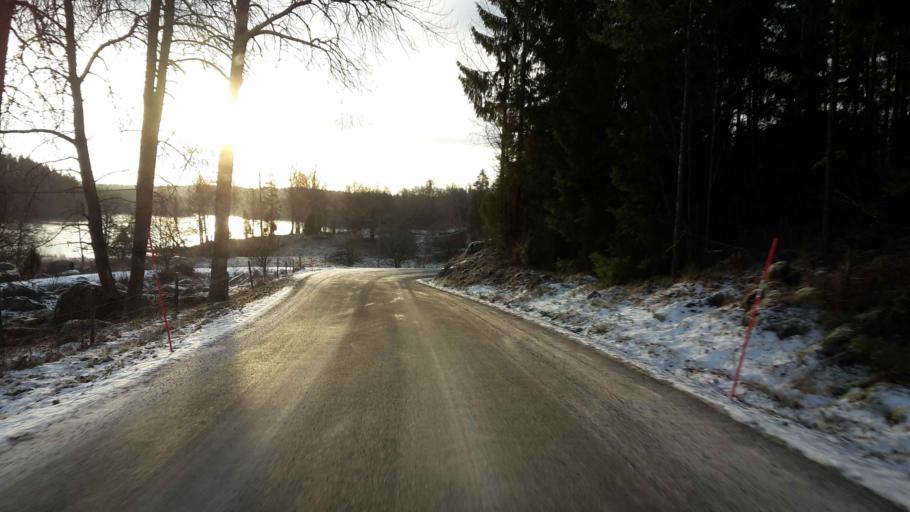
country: SE
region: OEstergoetland
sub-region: Atvidabergs Kommun
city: Atvidaberg
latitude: 58.2582
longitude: 16.1009
